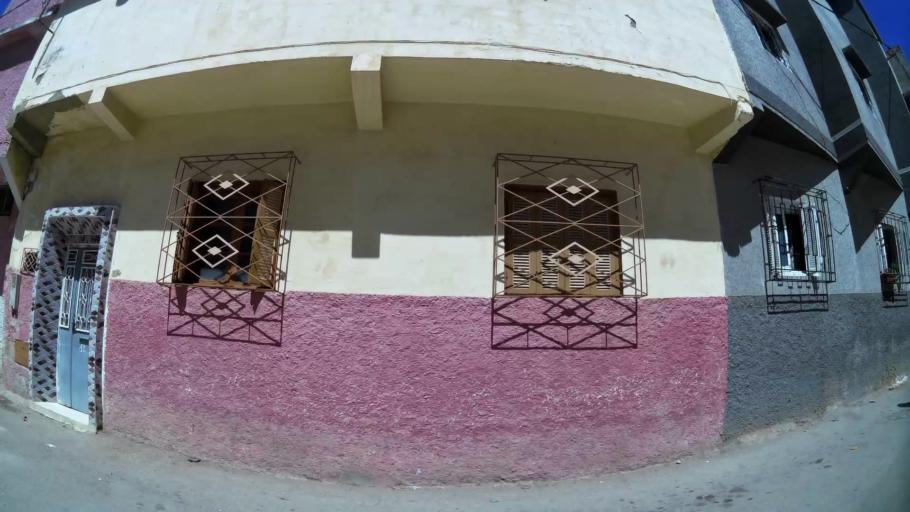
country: MA
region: Meknes-Tafilalet
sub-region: Meknes
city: Meknes
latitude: 33.8707
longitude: -5.5628
